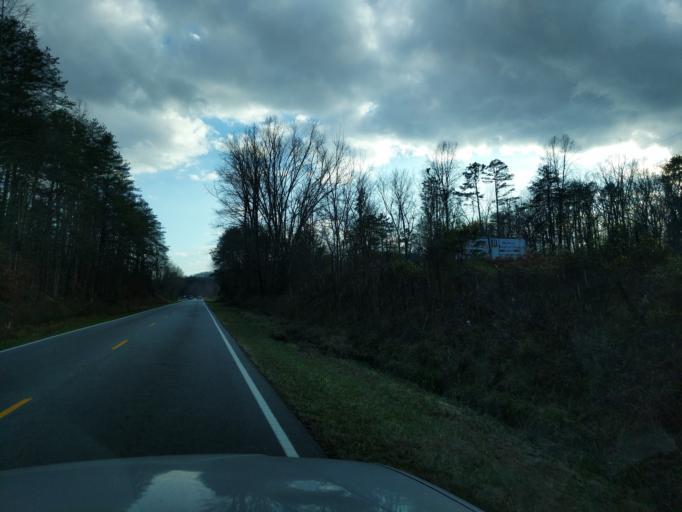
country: US
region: North Carolina
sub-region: McDowell County
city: West Marion
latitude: 35.5943
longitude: -81.9836
